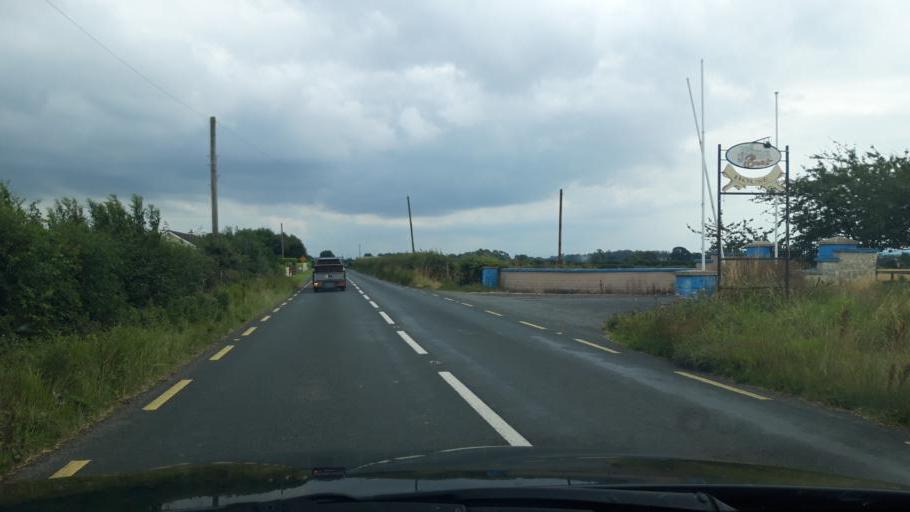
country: IE
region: Leinster
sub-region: Kildare
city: Athy
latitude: 53.0239
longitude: -7.0086
